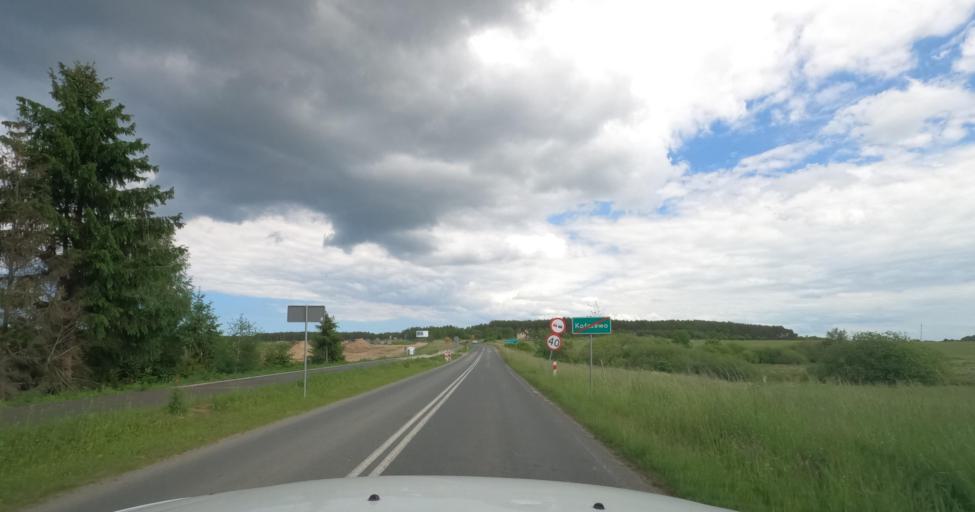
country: PL
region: West Pomeranian Voivodeship
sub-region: Powiat kamienski
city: Wolin
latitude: 53.9702
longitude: 14.6192
